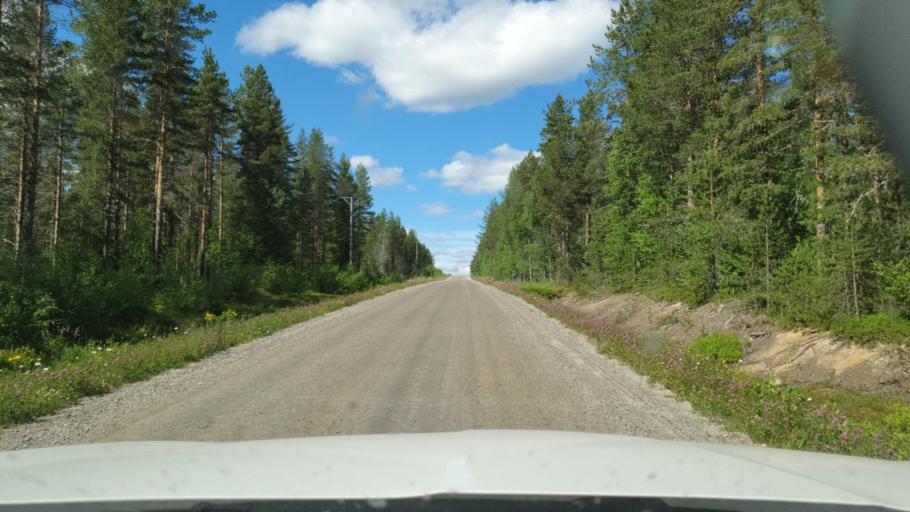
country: SE
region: Norrbotten
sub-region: Pitea Kommun
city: Roknas
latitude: 65.1609
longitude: 21.1508
